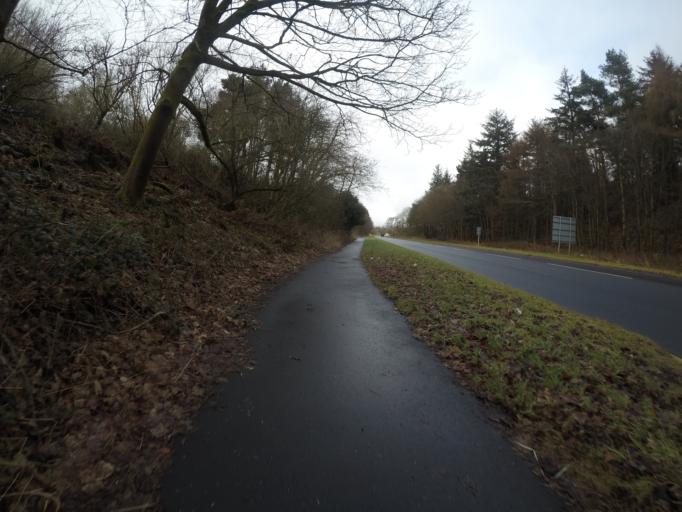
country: GB
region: Scotland
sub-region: North Ayrshire
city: Fairlie
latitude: 55.7295
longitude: -4.8653
